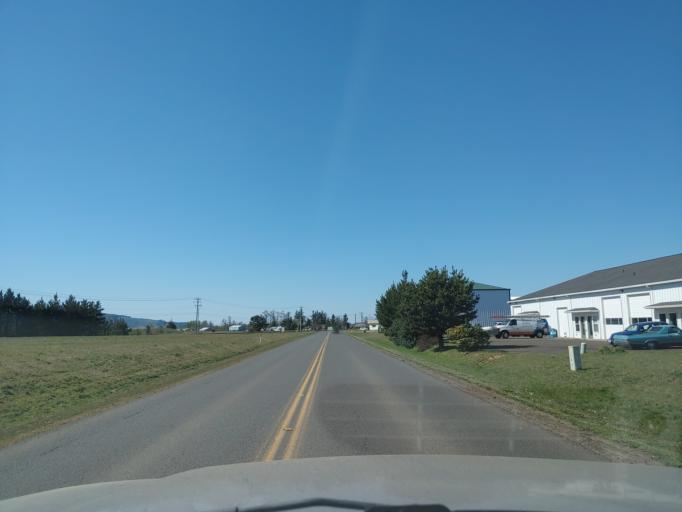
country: US
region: Oregon
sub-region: Tillamook County
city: Tillamook
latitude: 45.4237
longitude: -123.7990
